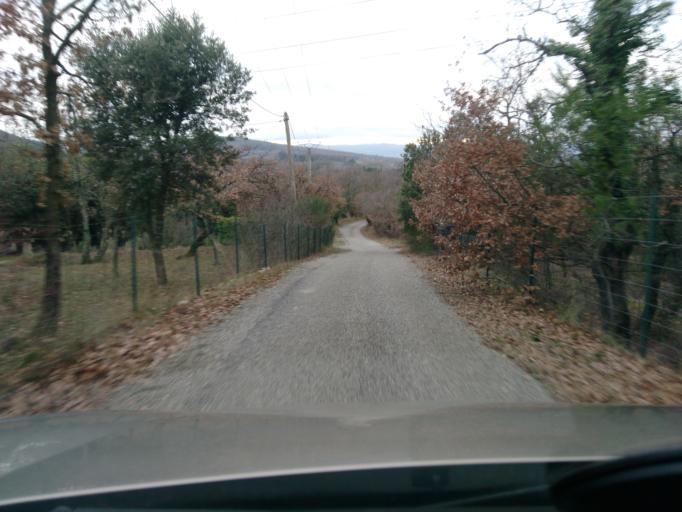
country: FR
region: Rhone-Alpes
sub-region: Departement de la Drome
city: Montboucher-sur-Jabron
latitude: 44.5352
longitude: 4.8224
